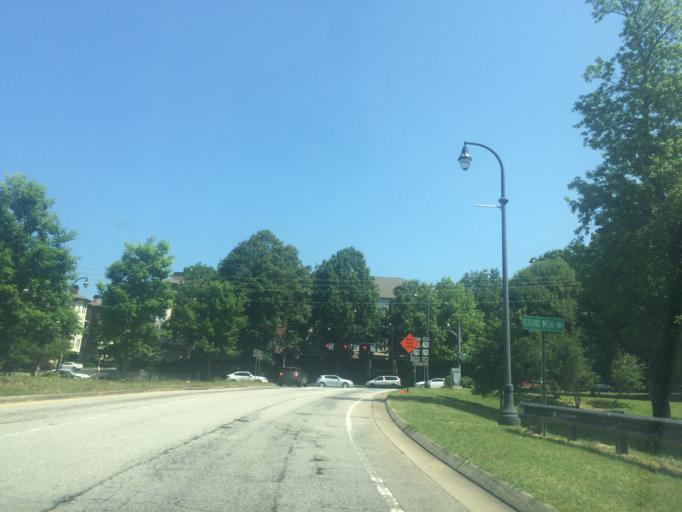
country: US
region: Georgia
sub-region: DeKalb County
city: Druid Hills
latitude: 33.7731
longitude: -84.3599
